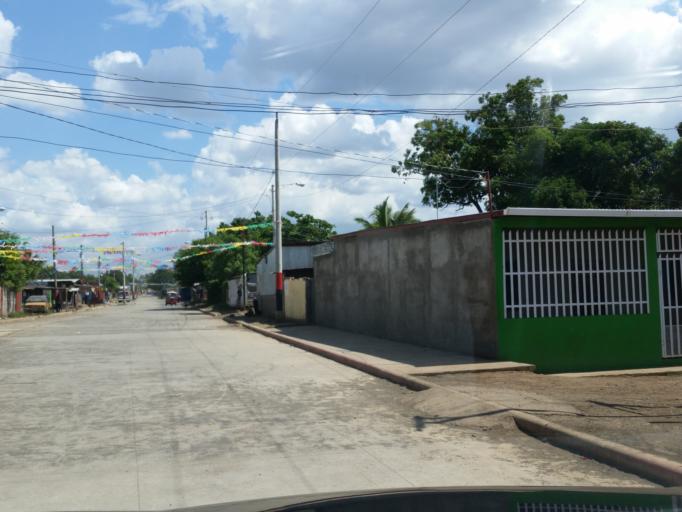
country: NI
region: Managua
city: Managua
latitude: 12.1616
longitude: -86.2029
